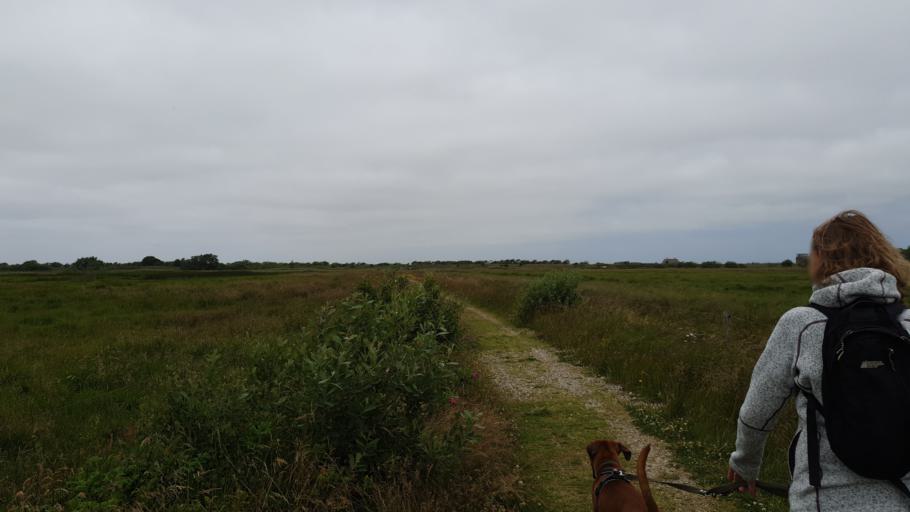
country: DK
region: Central Jutland
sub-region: Ringkobing-Skjern Kommune
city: Skjern
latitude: 55.9144
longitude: 8.4072
